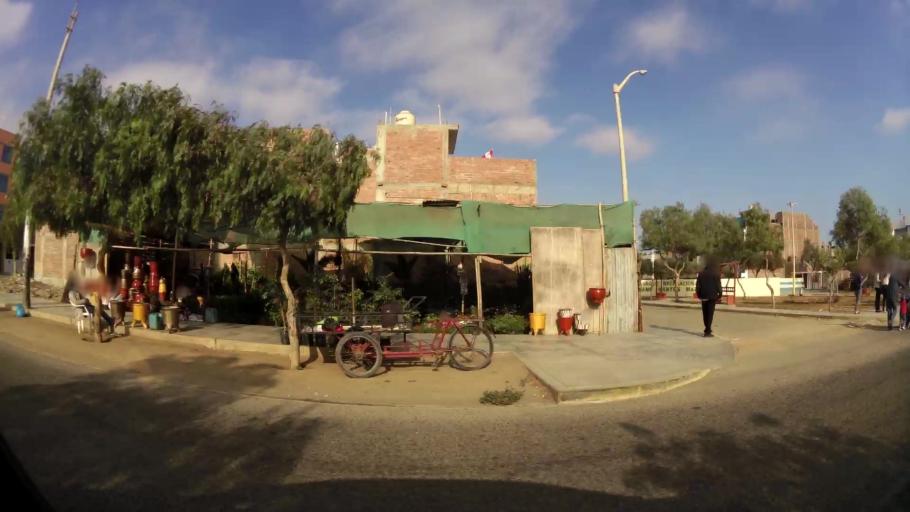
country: PE
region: La Libertad
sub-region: Provincia de Trujillo
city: La Esperanza
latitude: -8.0978
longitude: -79.0485
